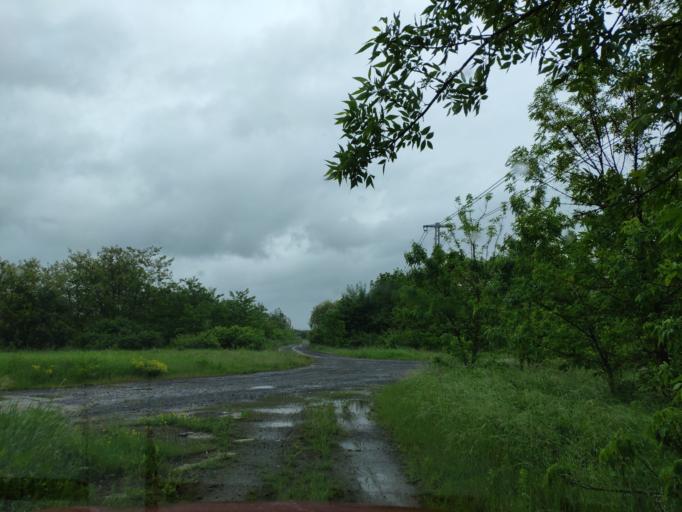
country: SK
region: Kosicky
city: Cierna nad Tisou
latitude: 48.4271
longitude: 22.0995
